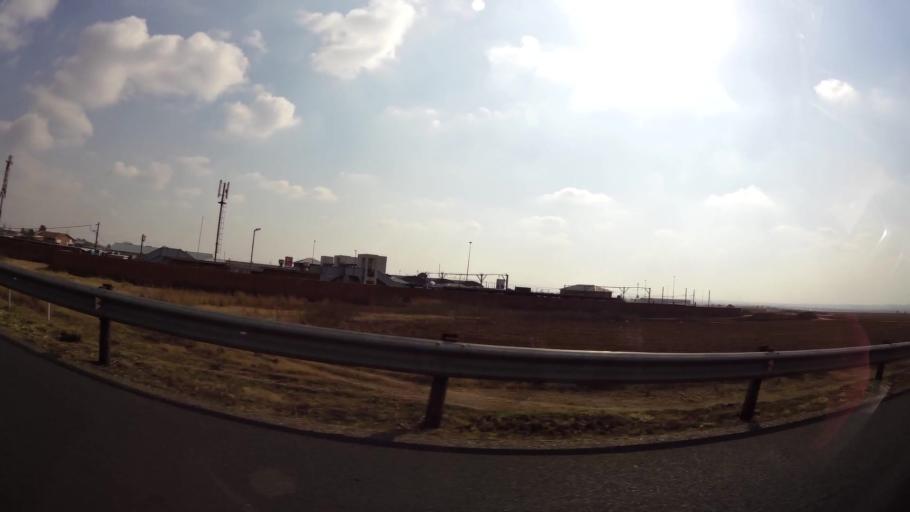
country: ZA
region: Gauteng
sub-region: Ekurhuleni Metropolitan Municipality
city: Springs
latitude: -26.1572
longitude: 28.4251
